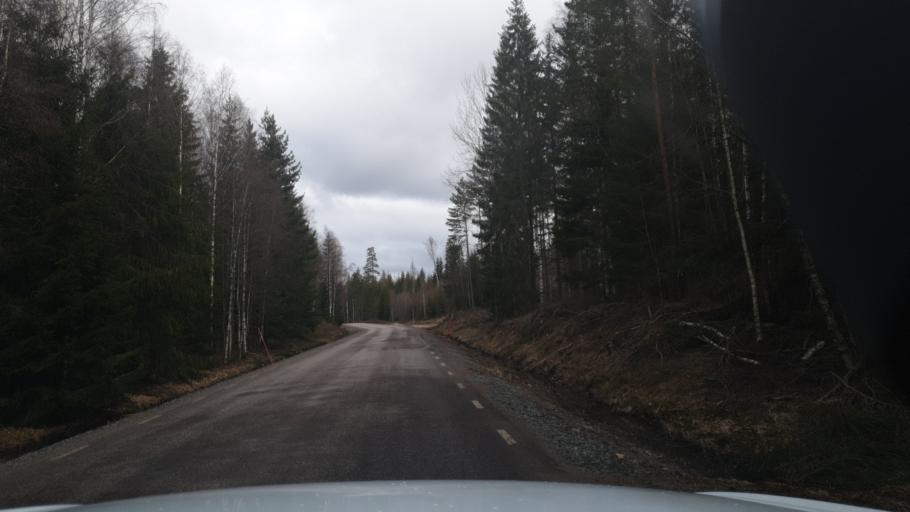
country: SE
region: Vaermland
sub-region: Grums Kommun
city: Slottsbron
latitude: 59.4882
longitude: 12.8831
